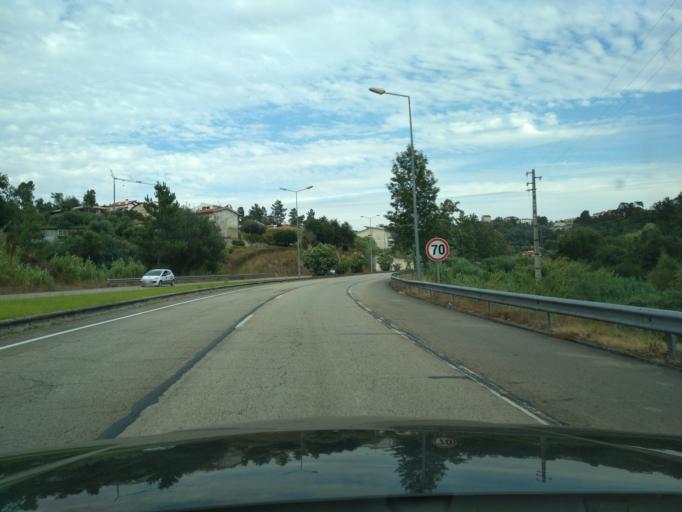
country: PT
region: Coimbra
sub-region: Coimbra
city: Coimbra
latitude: 40.2260
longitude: -8.4086
